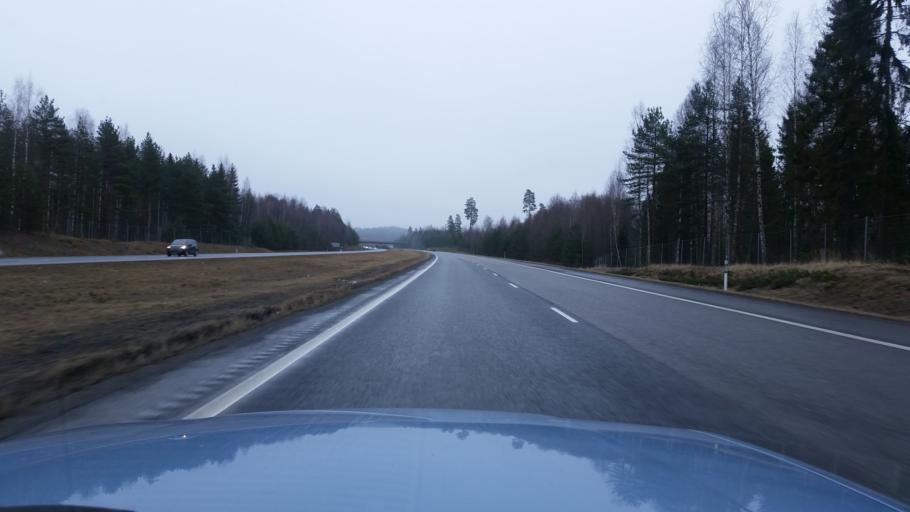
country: FI
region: Haeme
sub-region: Haemeenlinna
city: Parola
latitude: 61.0722
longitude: 24.2906
